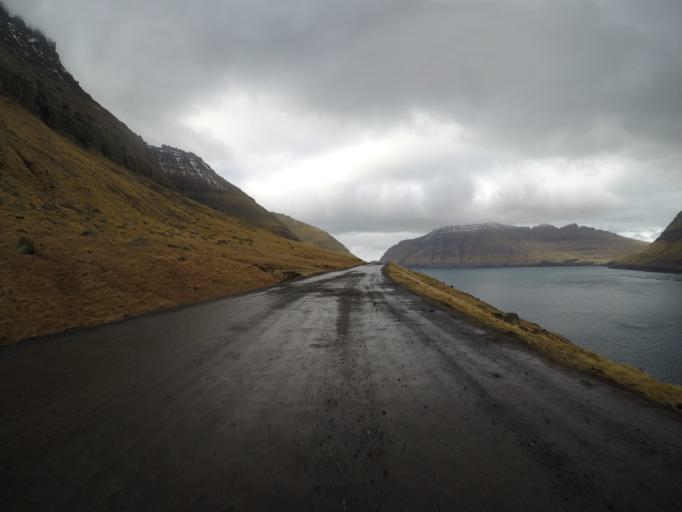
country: FO
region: Nordoyar
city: Klaksvik
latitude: 62.3358
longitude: -6.5783
